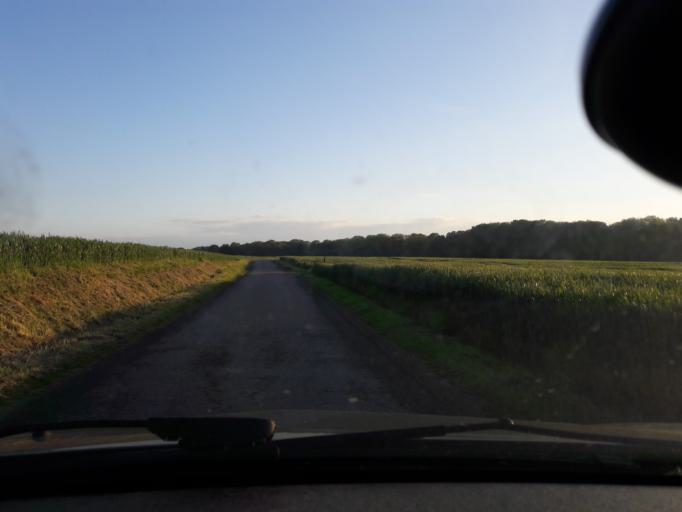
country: FR
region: Nord-Pas-de-Calais
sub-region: Departement du Nord
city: Marpent
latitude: 50.2773
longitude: 4.0636
